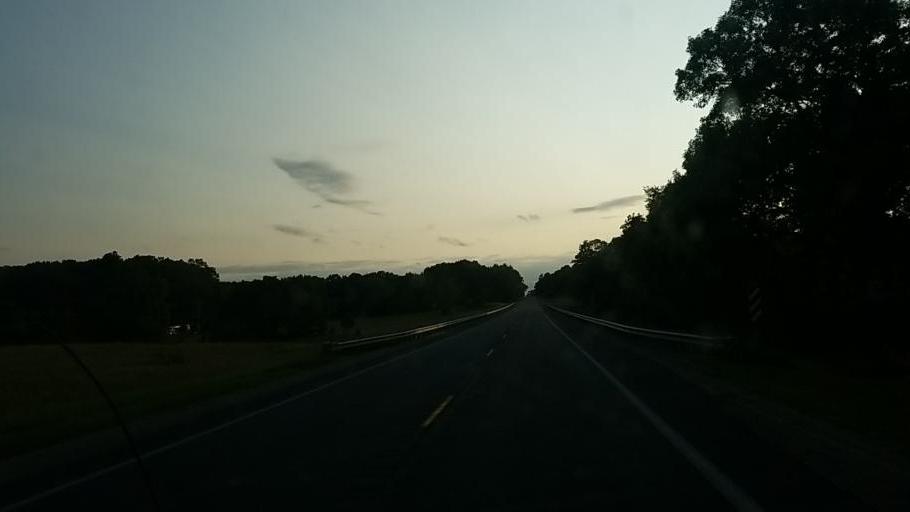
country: US
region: Michigan
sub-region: Montcalm County
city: Howard City
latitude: 43.3958
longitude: -85.5854
